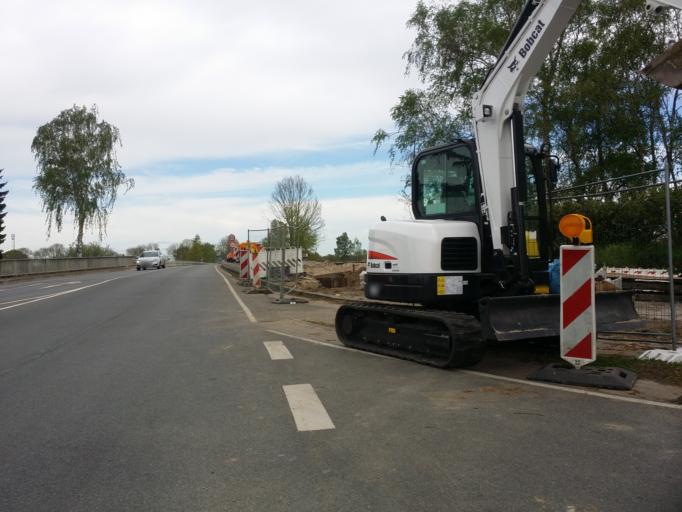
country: DE
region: Lower Saxony
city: Lemwerder
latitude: 53.1469
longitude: 8.5479
